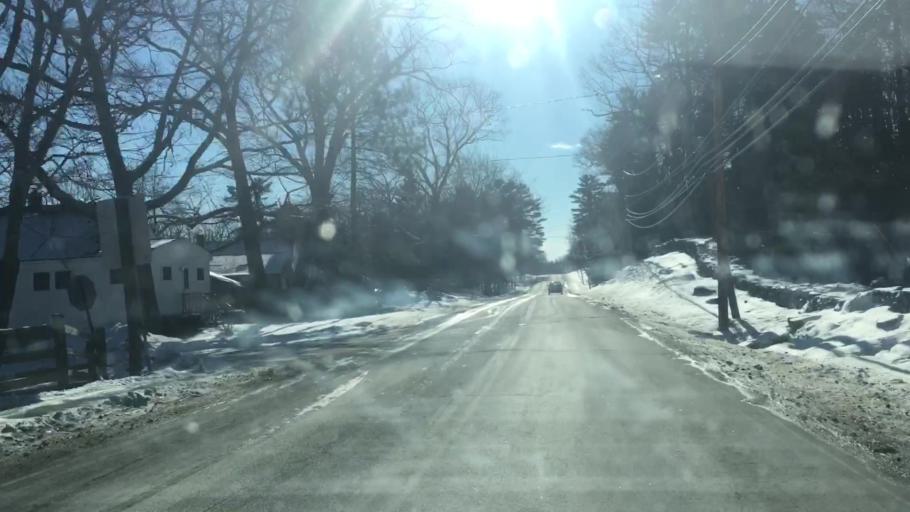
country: US
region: Maine
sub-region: Hancock County
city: Ellsworth
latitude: 44.5372
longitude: -68.4306
